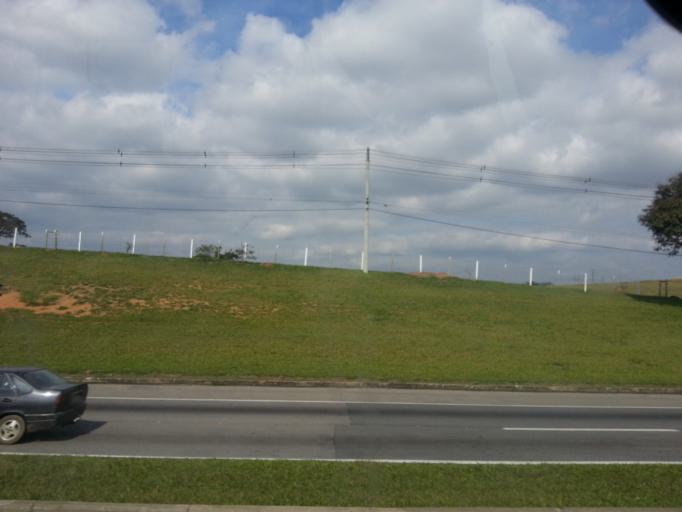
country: BR
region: Sao Paulo
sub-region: Cacapava
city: Cacapava
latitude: -23.1416
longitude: -45.7649
